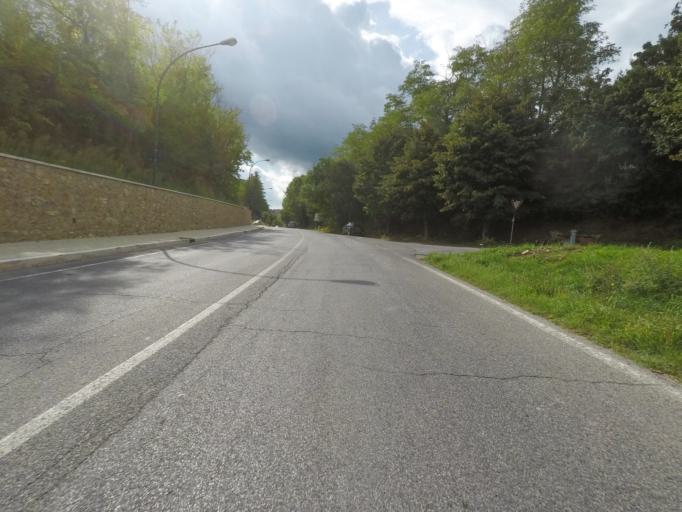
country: IT
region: Tuscany
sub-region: Provincia di Siena
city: Montepulciano
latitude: 43.1072
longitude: 11.7862
